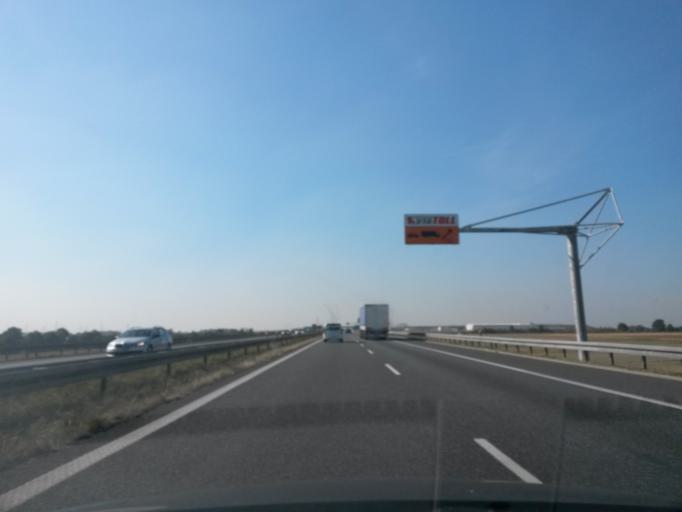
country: PL
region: Silesian Voivodeship
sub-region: Gliwice
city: Gliwice
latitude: 50.2590
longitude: 18.6863
